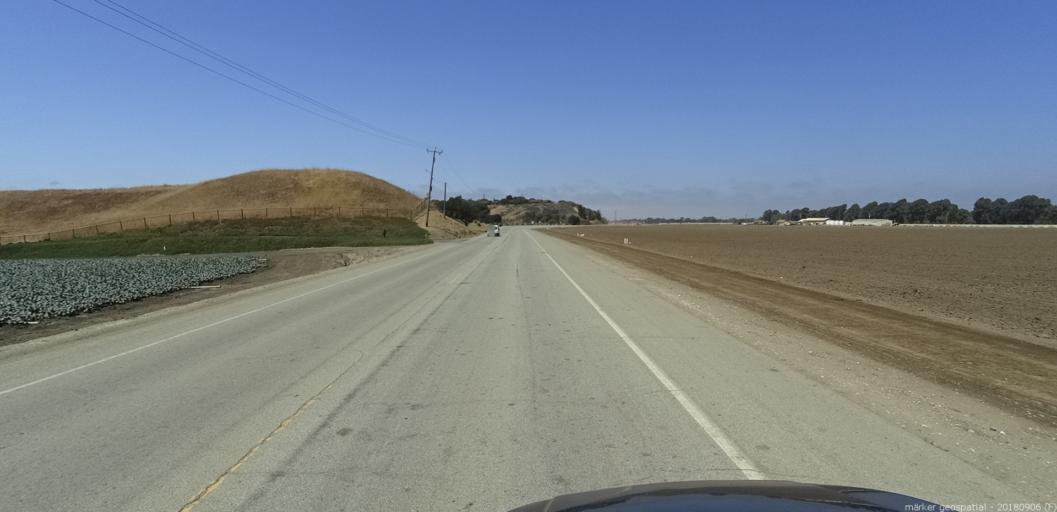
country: US
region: California
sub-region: Monterey County
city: Salinas
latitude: 36.6362
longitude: -121.7010
